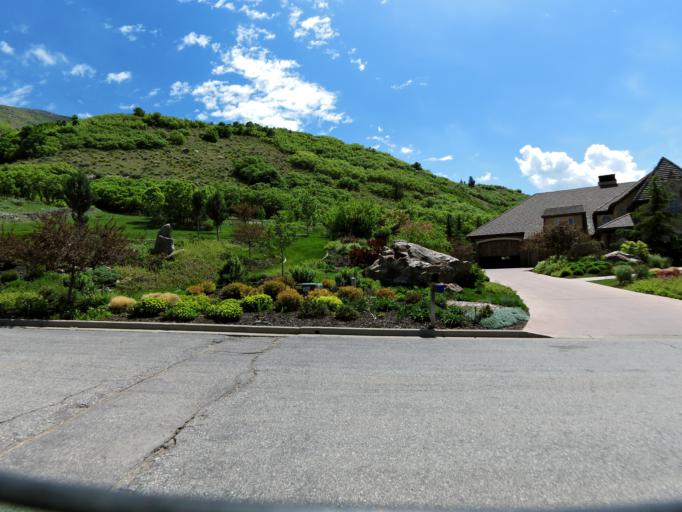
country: US
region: Utah
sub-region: Weber County
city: Uintah
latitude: 41.1804
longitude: -111.9307
